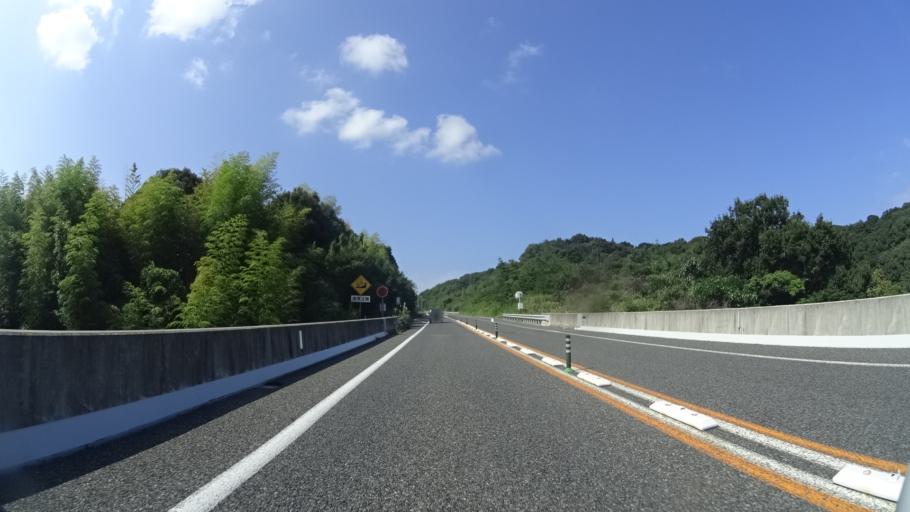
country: JP
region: Shimane
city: Hamada
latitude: 34.9176
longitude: 132.1317
